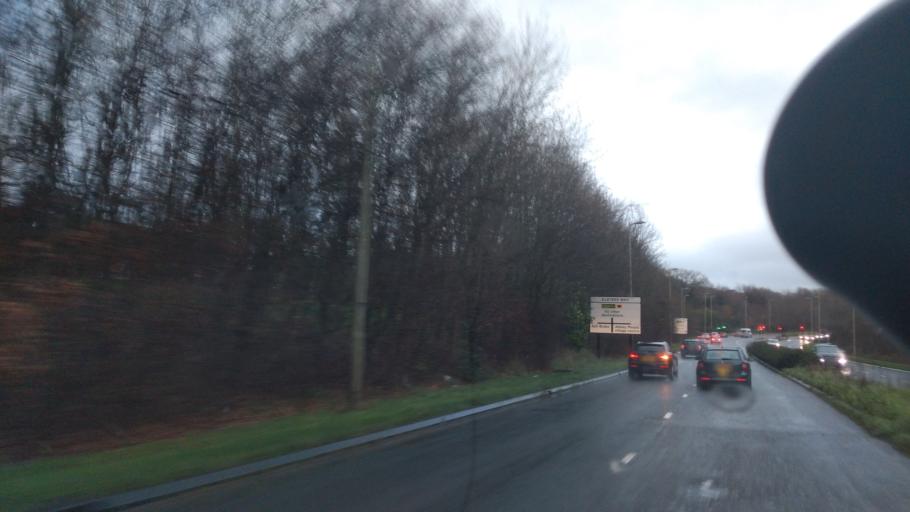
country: GB
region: England
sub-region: Borough of Swindon
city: Broad Blunsdon
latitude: 51.6000
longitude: -1.7994
